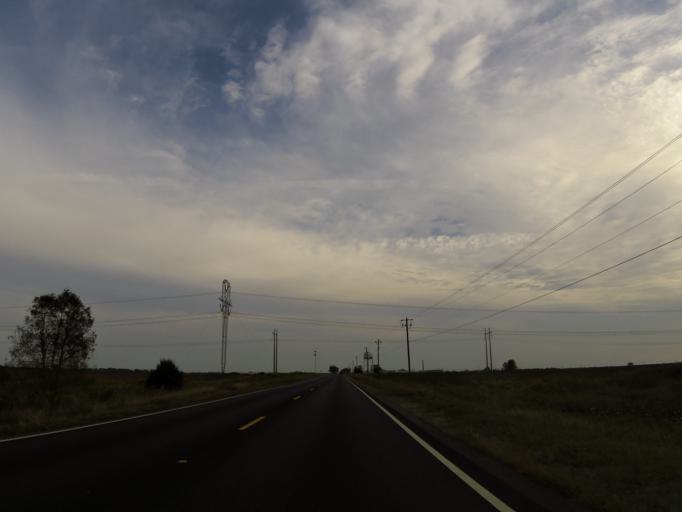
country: US
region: Alabama
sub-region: Escambia County
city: Atmore
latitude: 31.1677
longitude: -87.4637
